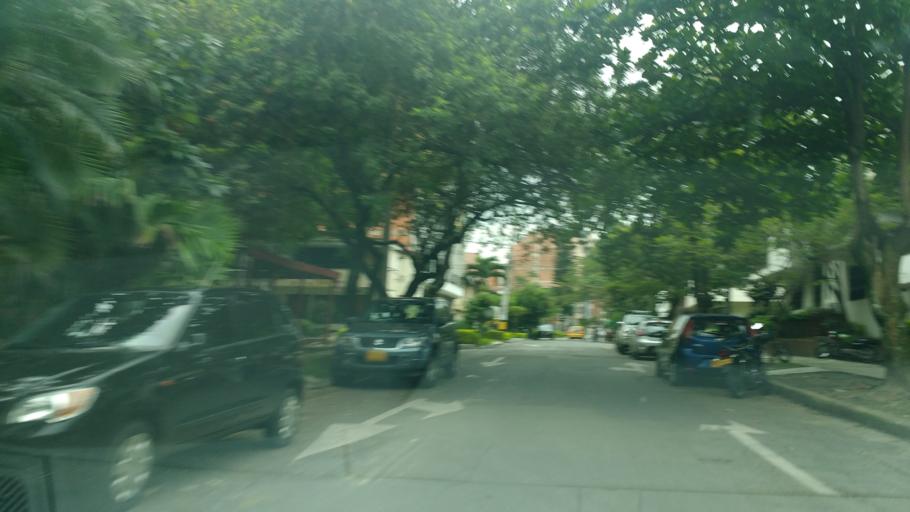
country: CO
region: Antioquia
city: Medellin
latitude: 6.2532
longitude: -75.5926
